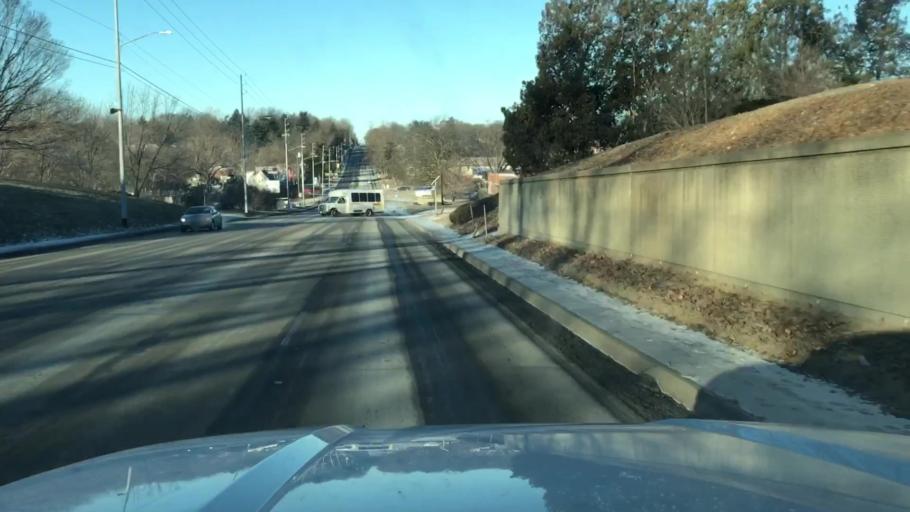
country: US
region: Missouri
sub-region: Buchanan County
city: Saint Joseph
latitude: 39.7770
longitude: -94.8140
